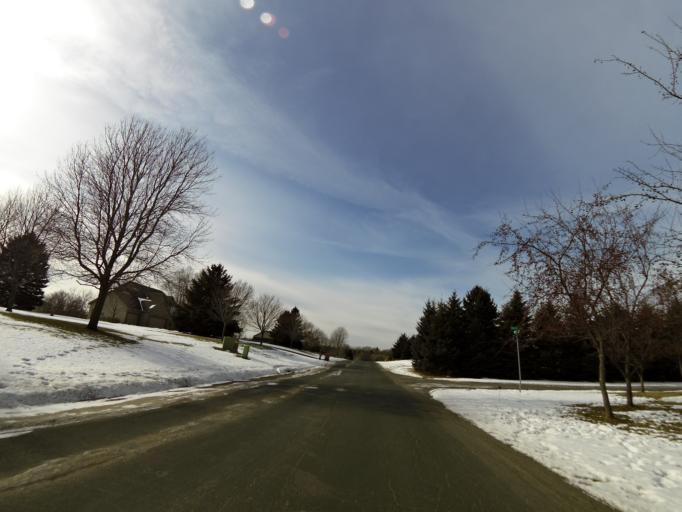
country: US
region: Minnesota
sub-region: Washington County
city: Lake Elmo
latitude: 44.9835
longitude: -92.8578
